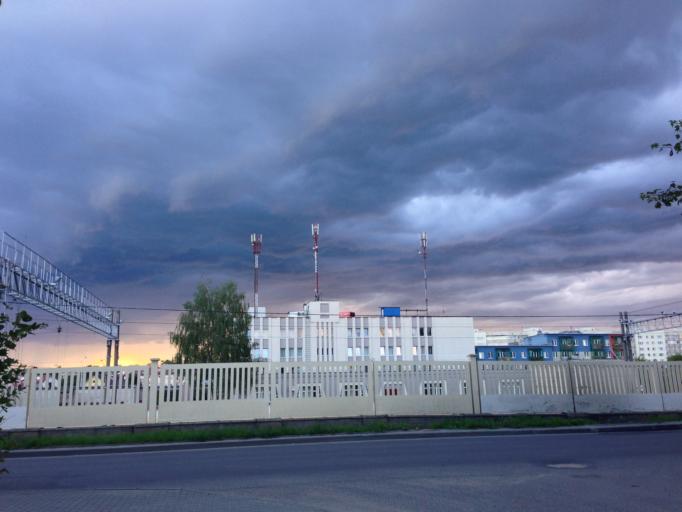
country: BY
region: Grodnenskaya
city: Hrodna
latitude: 53.6847
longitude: 23.8485
